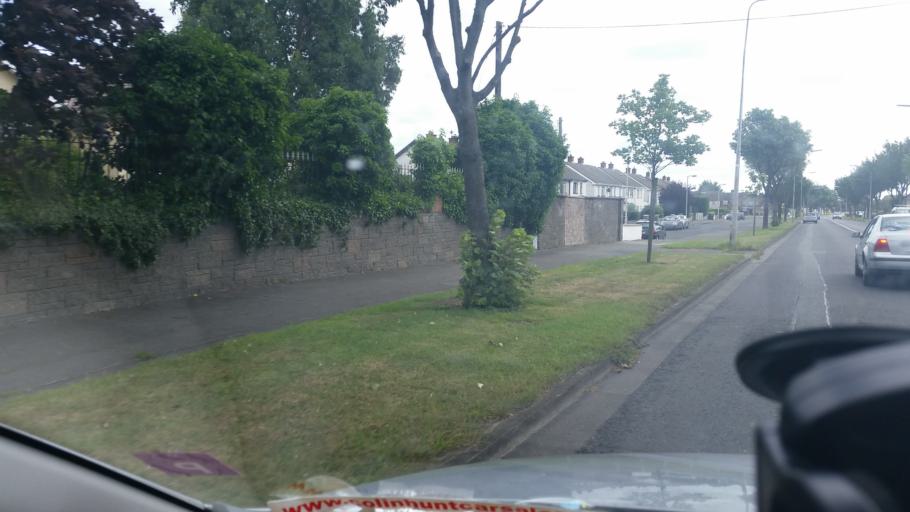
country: IE
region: Leinster
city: Raheny
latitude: 53.3912
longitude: -6.1749
